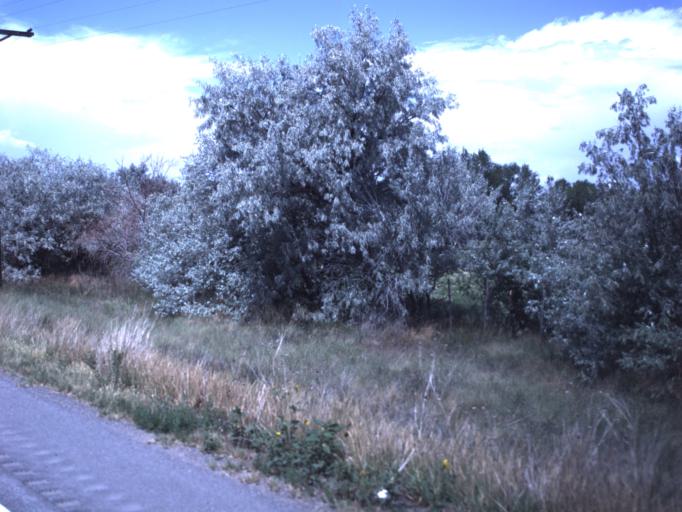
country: US
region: Utah
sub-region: Duchesne County
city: Roosevelt
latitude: 40.3020
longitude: -109.8015
